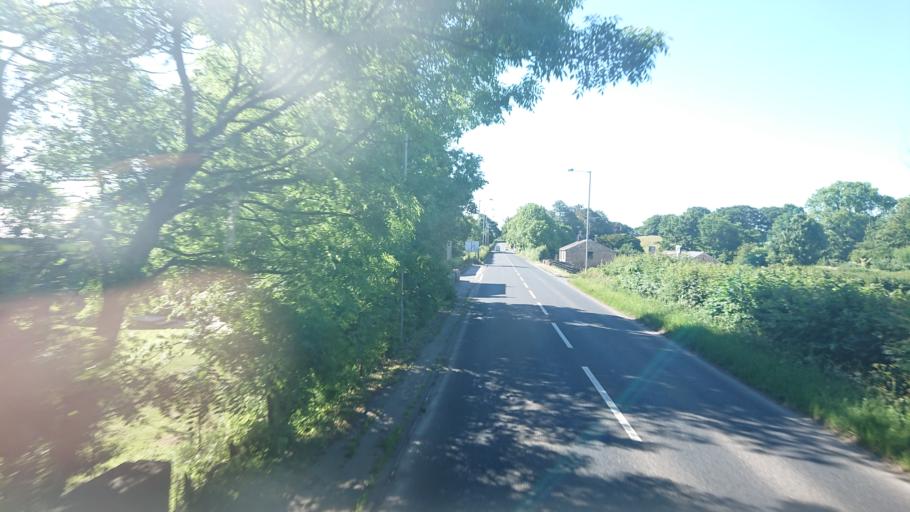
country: GB
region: England
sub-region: Lancashire
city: Bay Horse
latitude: 53.9680
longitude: -2.7802
